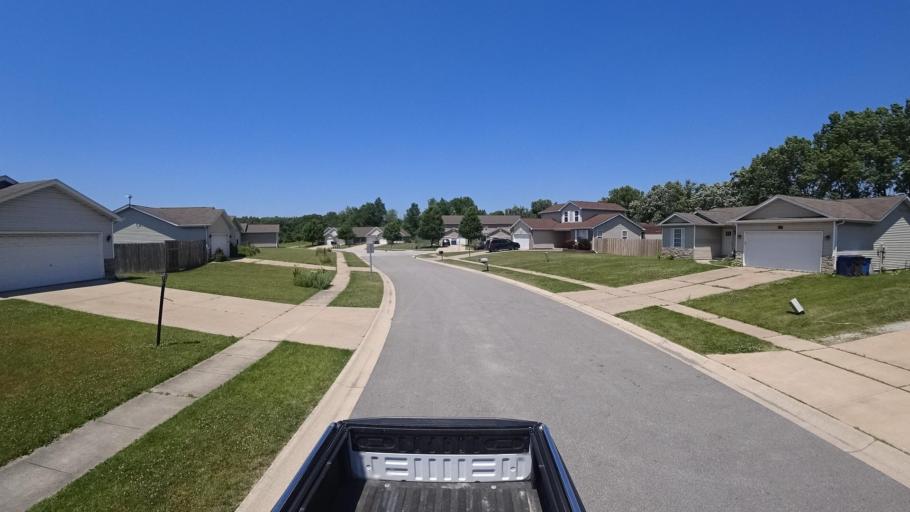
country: US
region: Indiana
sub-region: Porter County
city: Burns Harbor
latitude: 41.6033
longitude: -87.1352
